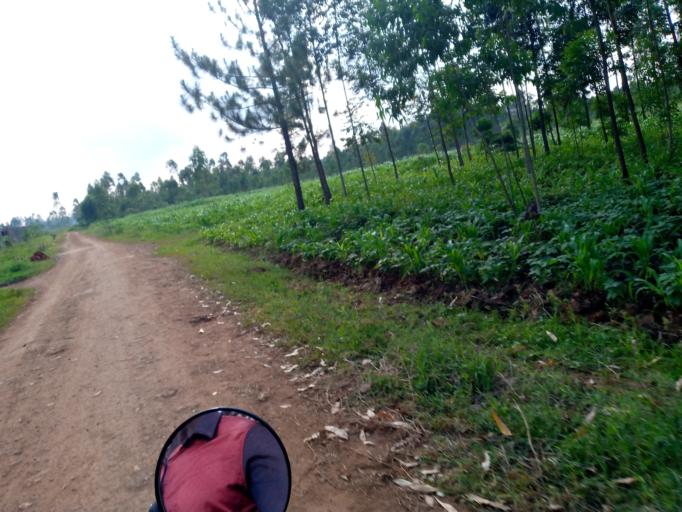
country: UG
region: Eastern Region
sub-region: Mbale District
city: Mbale
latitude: 1.0591
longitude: 34.1689
